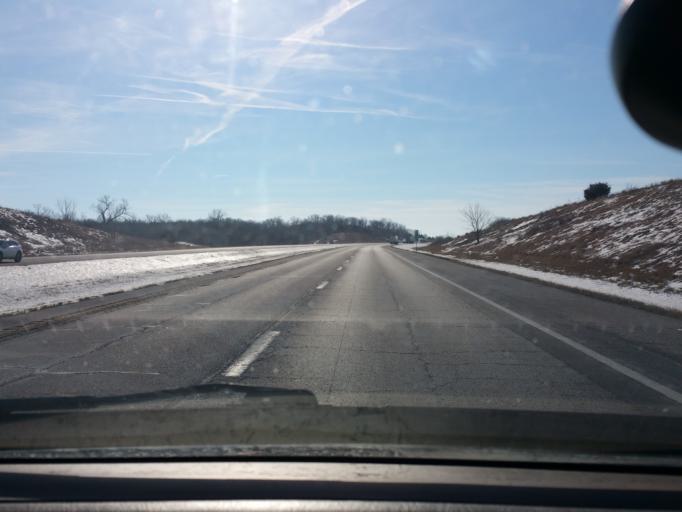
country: US
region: Missouri
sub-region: Harrison County
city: Bethany
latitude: 40.1847
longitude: -94.0149
